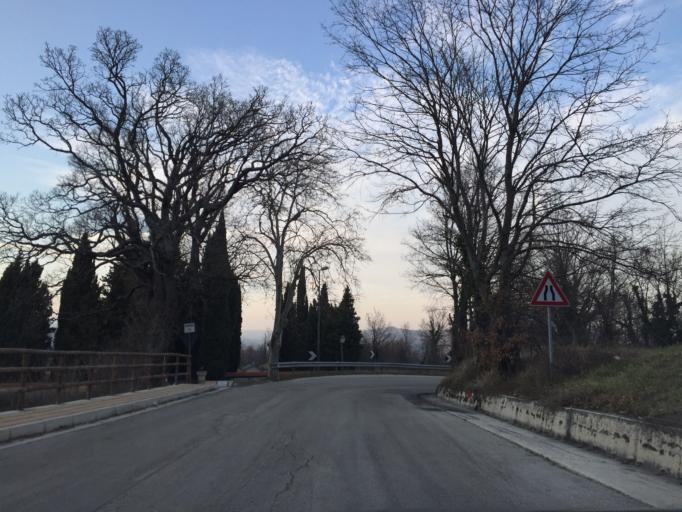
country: IT
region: Molise
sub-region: Provincia di Campobasso
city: Guardiaregia
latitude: 41.4403
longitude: 14.5459
